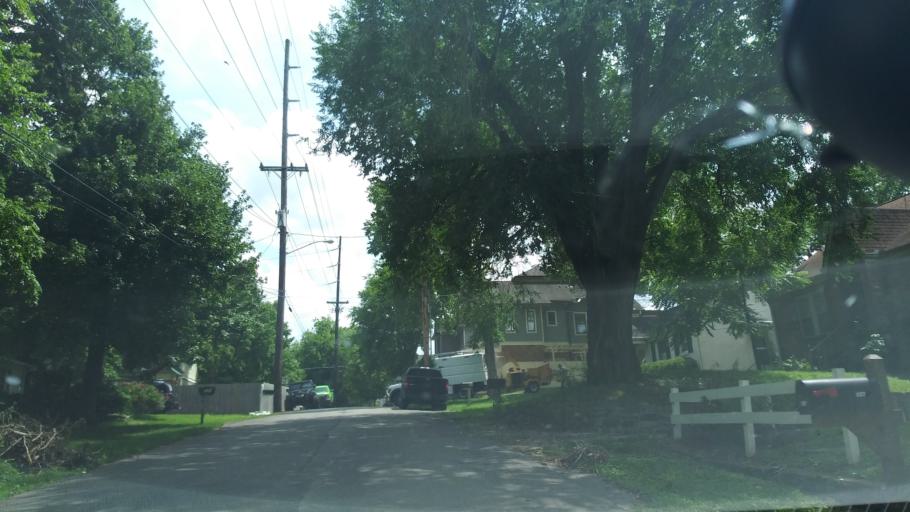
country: US
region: Tennessee
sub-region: Davidson County
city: Belle Meade
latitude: 36.1401
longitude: -86.8384
